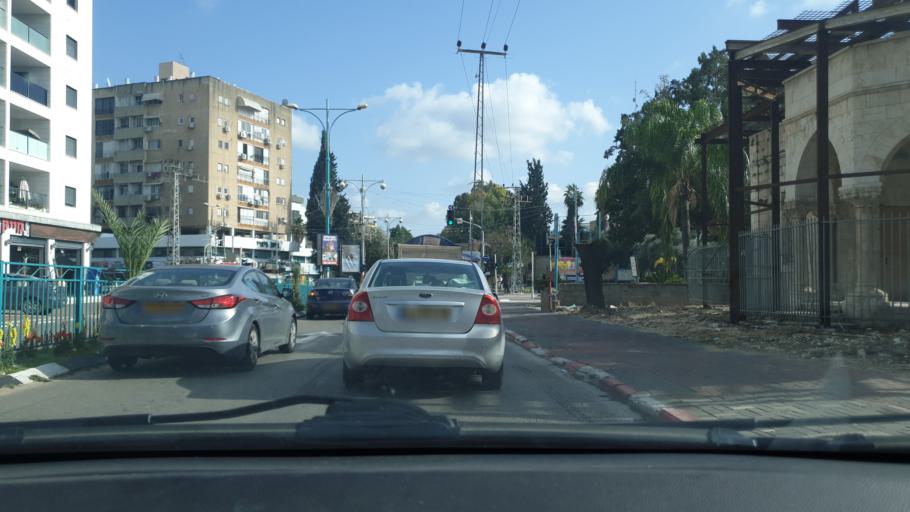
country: IL
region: Central District
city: Ramla
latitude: 31.9326
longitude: 34.8686
